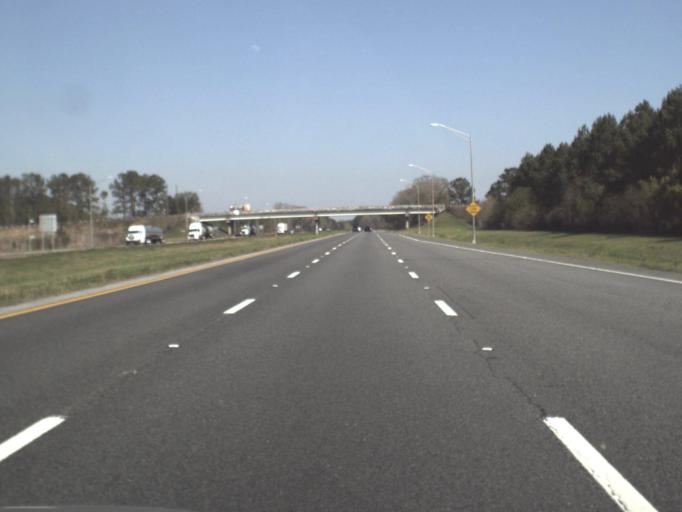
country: US
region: Florida
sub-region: Jackson County
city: Sneads
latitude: 30.6398
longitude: -84.9771
